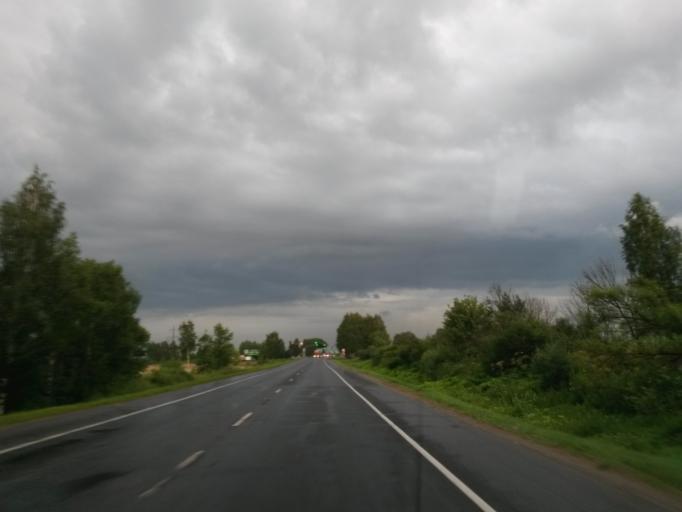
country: RU
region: Jaroslavl
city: Yaroslavl
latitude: 57.5602
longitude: 39.8505
